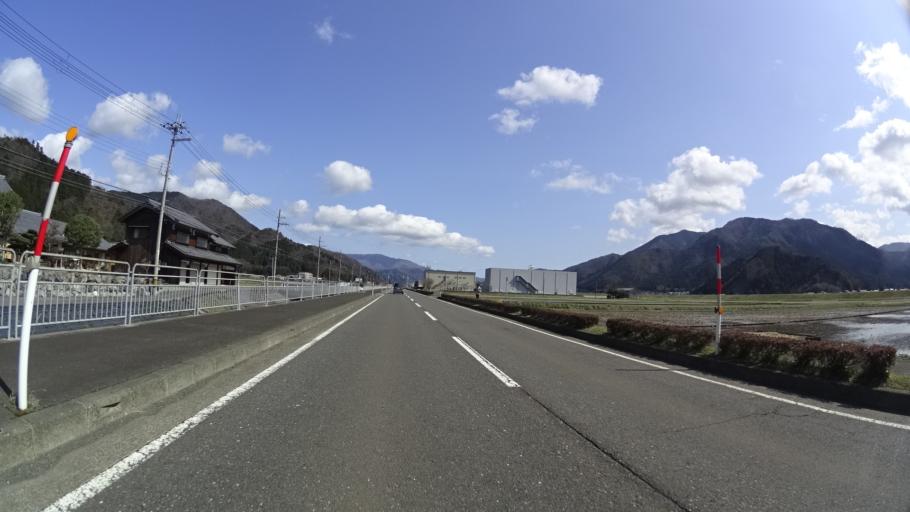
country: JP
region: Fukui
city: Obama
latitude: 35.4767
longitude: 135.8216
